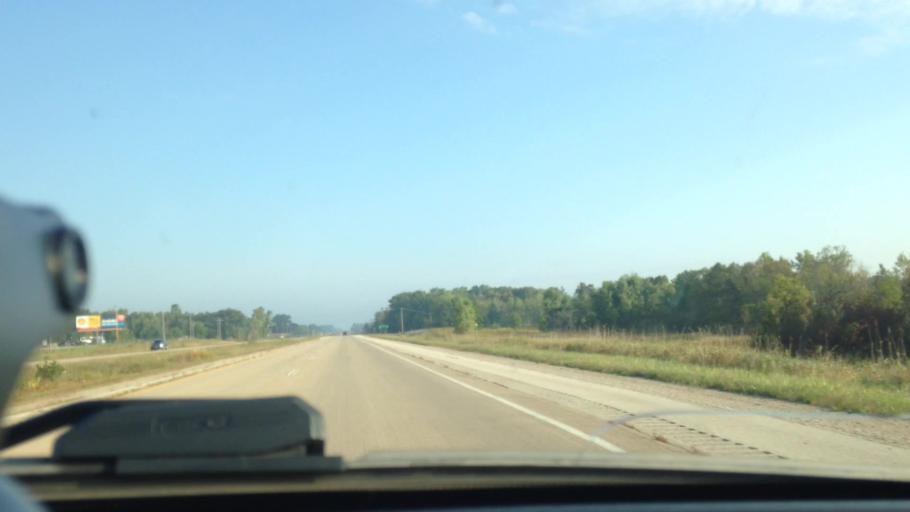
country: US
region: Wisconsin
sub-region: Oconto County
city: Oconto Falls
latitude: 44.9972
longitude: -88.0450
